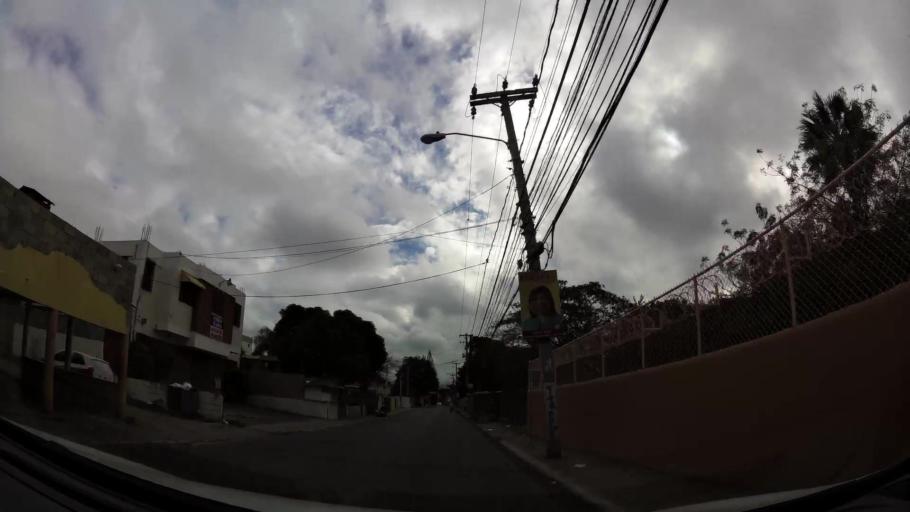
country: DO
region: Santiago
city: Santiago de los Caballeros
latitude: 19.4606
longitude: -70.6592
